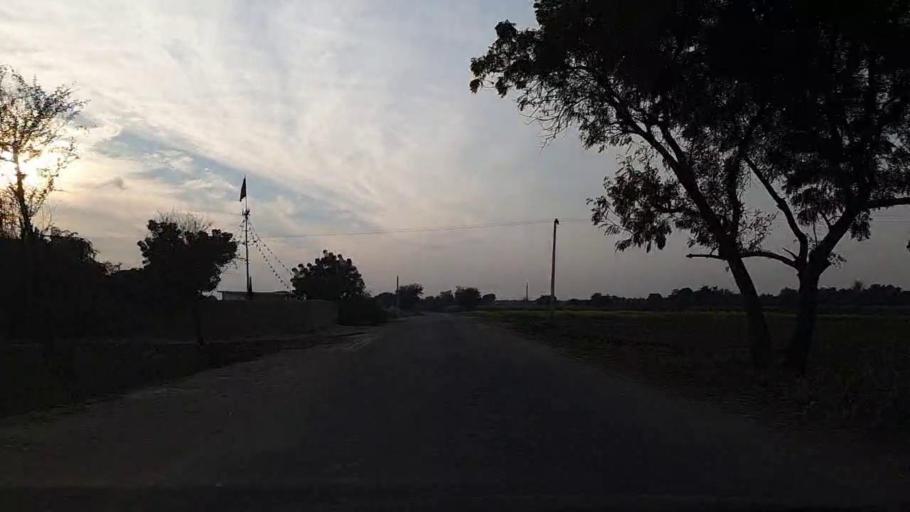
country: PK
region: Sindh
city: Nawabshah
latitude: 26.4032
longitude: 68.4854
